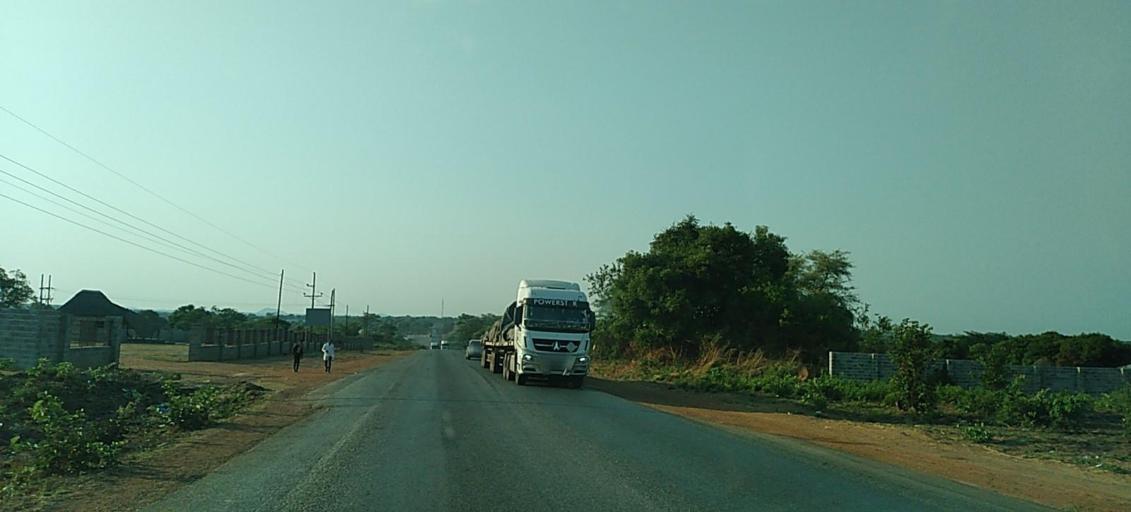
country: ZM
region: Copperbelt
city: Luanshya
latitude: -13.2947
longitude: 28.6853
